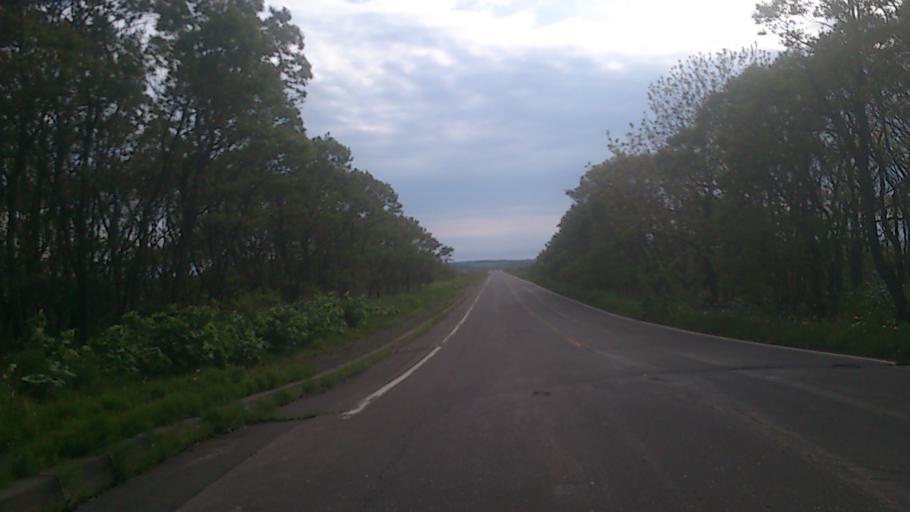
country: JP
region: Hokkaido
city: Makubetsu
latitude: 45.1123
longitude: 141.6999
